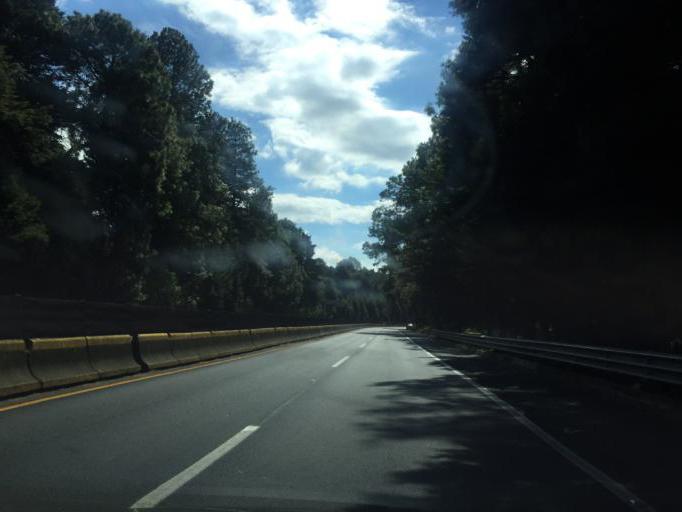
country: MX
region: Morelos
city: Tres Marias
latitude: 19.0401
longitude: -99.2304
